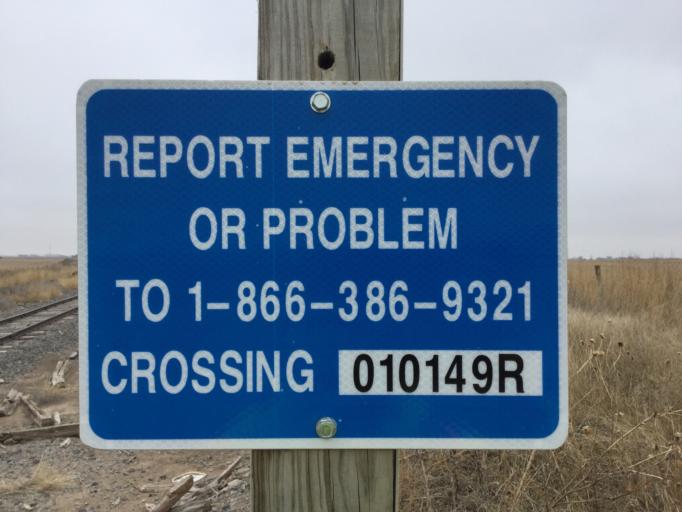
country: US
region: Kansas
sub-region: Edwards County
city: Kinsley
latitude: 38.1917
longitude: -99.4785
